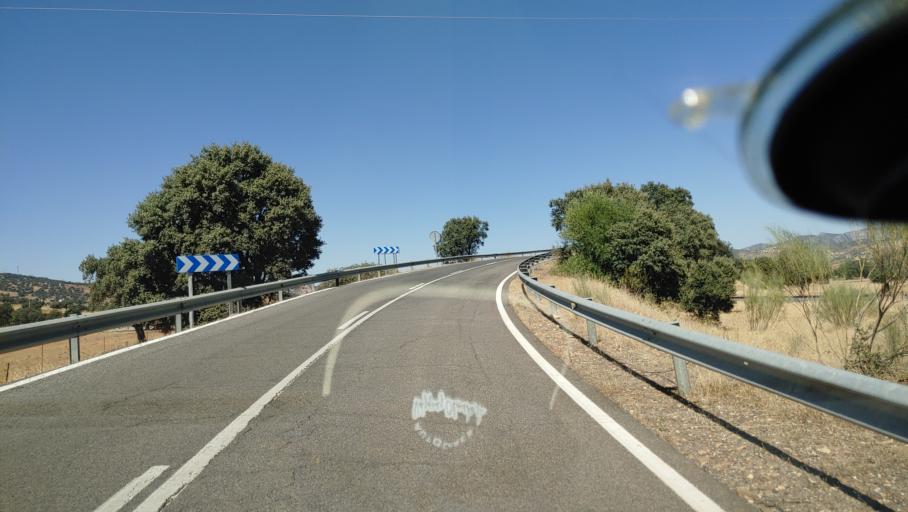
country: ES
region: Castille-La Mancha
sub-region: Provincia de Ciudad Real
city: Guadalmez
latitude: 38.7032
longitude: -4.9441
